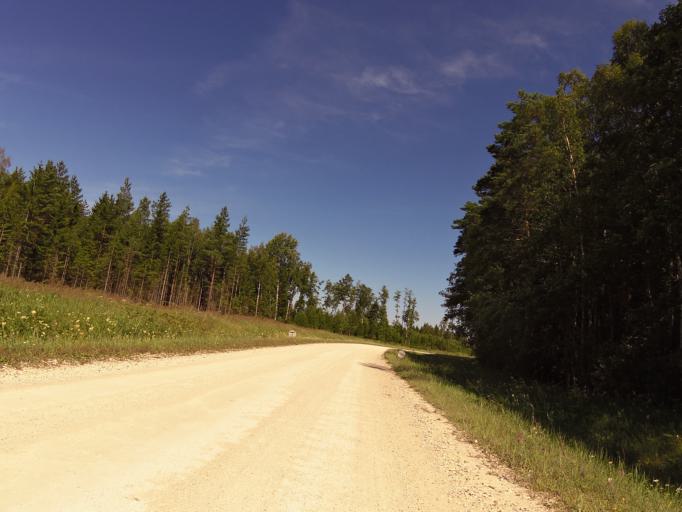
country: EE
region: Hiiumaa
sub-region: Kaerdla linn
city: Kardla
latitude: 58.9254
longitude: 22.3679
